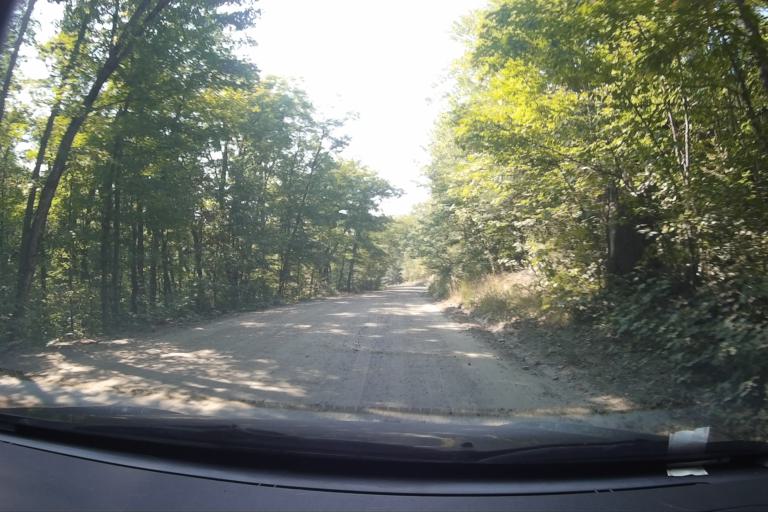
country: CA
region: Ontario
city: Huntsville
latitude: 45.5520
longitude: -78.6965
